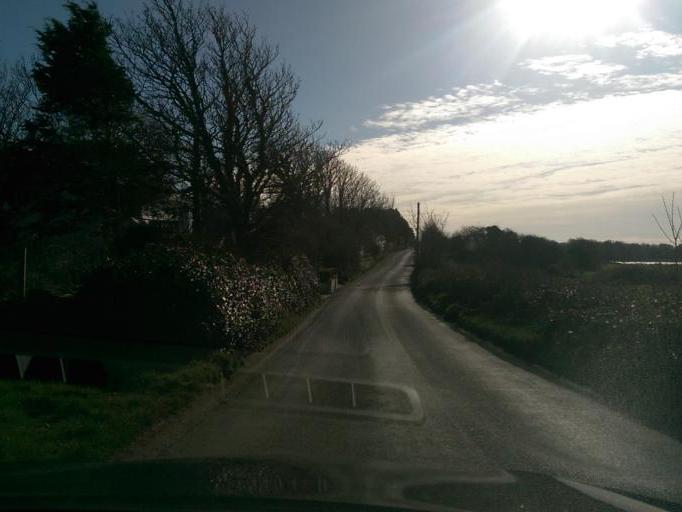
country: IE
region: Connaught
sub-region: County Galway
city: Oranmore
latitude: 53.2382
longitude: -8.9445
